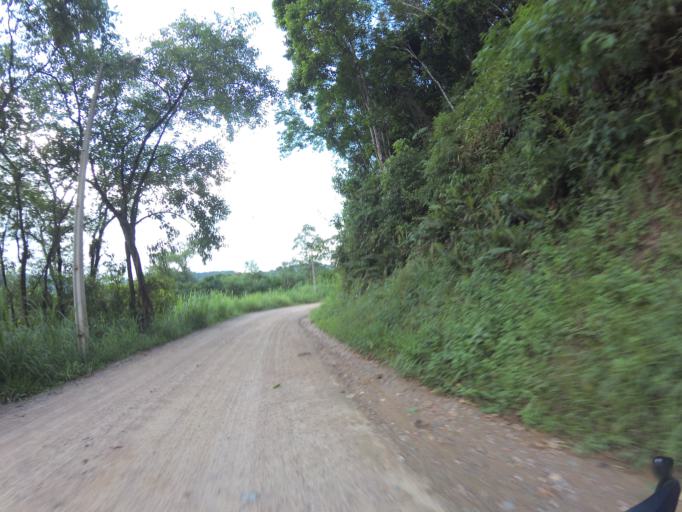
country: BR
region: Santa Catarina
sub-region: Pomerode
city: Pomerode
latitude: -26.8219
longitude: -49.1560
